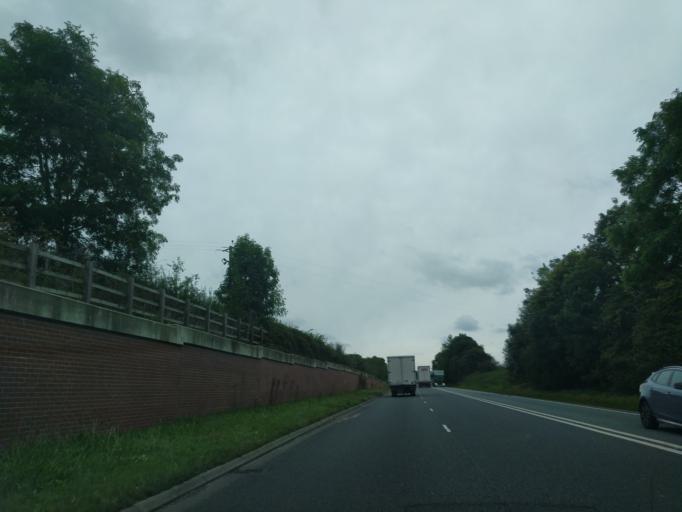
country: GB
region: England
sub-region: Cheshire East
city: Alsager
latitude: 53.0702
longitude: -2.3430
